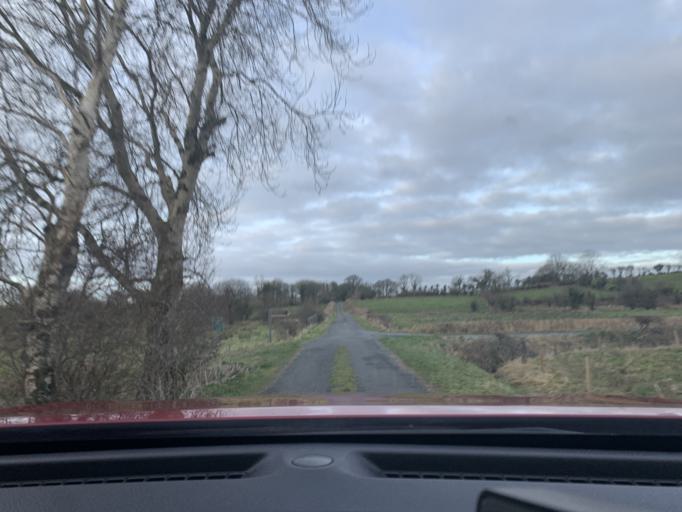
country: IE
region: Connaught
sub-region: Sligo
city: Ballymote
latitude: 54.0120
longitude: -8.5720
